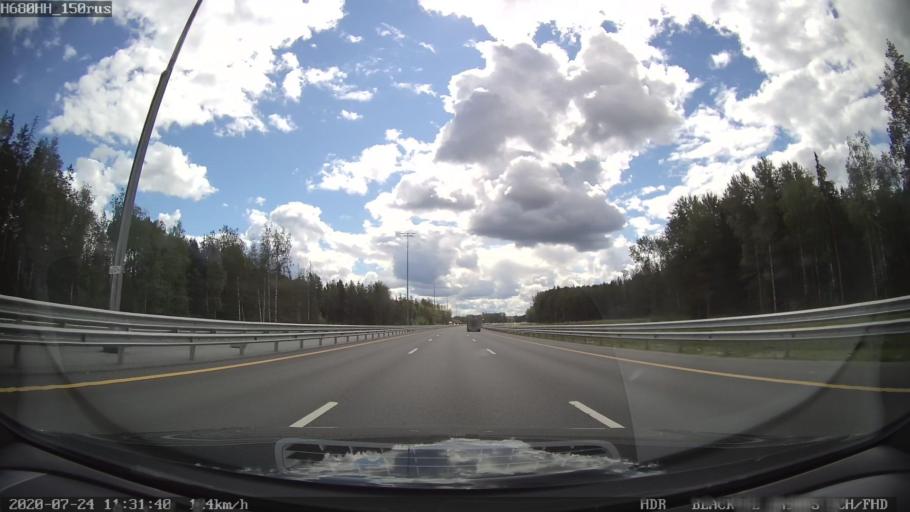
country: RU
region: Leningrad
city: Krasnyy Bor
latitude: 59.6532
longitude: 30.6427
